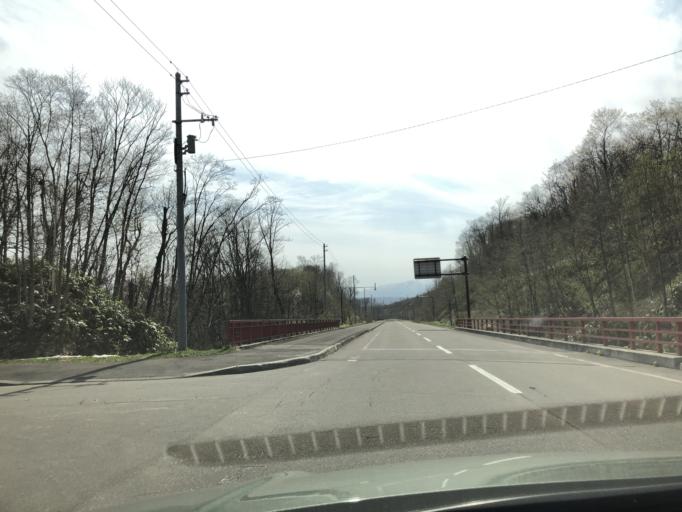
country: JP
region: Hokkaido
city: Akabira
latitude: 43.5933
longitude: 142.0401
